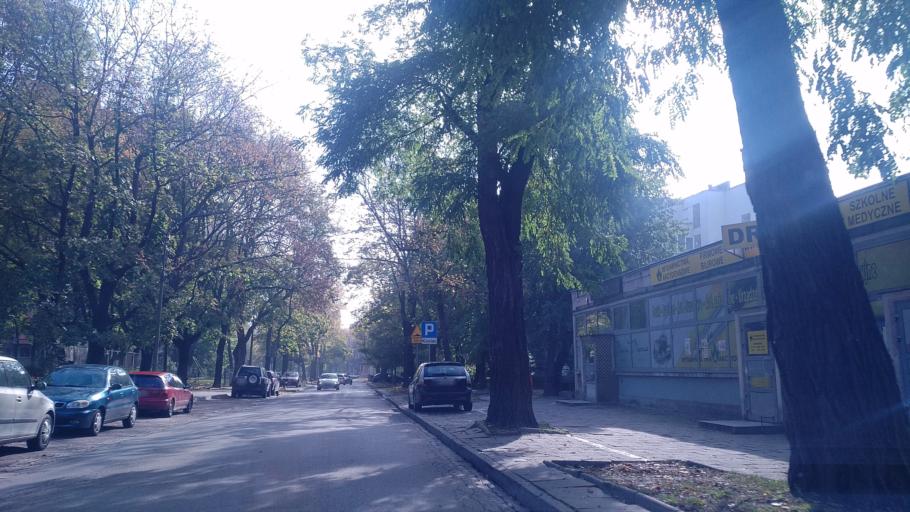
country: PL
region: Lesser Poland Voivodeship
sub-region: Krakow
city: Krakow
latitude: 50.0770
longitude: 19.9209
